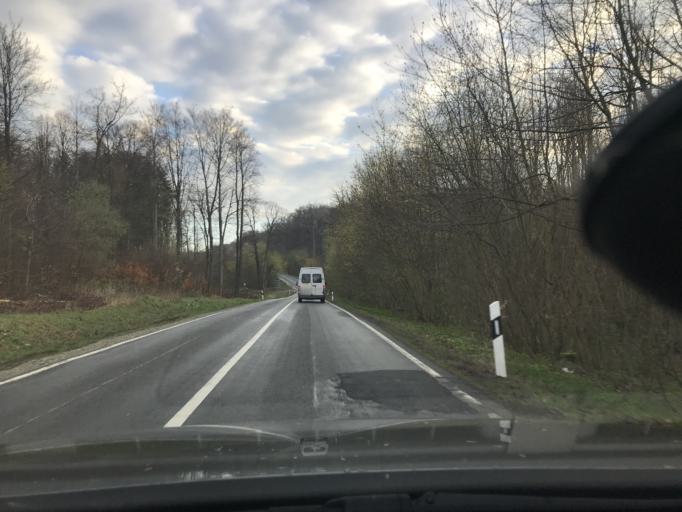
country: DE
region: Thuringia
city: Menteroda
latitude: 51.2893
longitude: 10.5504
